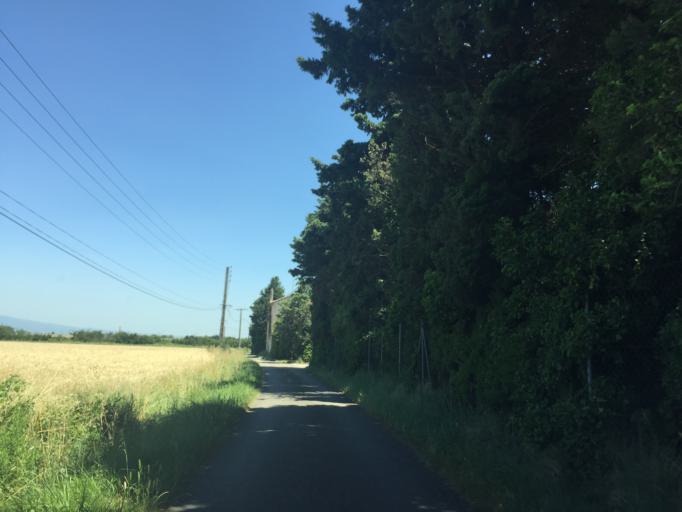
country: FR
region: Provence-Alpes-Cote d'Azur
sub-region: Departement du Vaucluse
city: Caderousse
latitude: 44.1103
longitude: 4.7661
